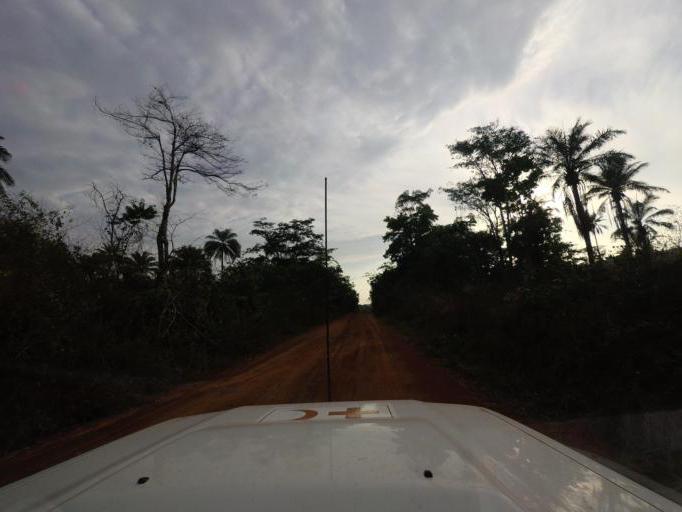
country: GN
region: Nzerekore
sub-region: Yomou
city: Yomou
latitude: 7.6549
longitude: -9.4495
